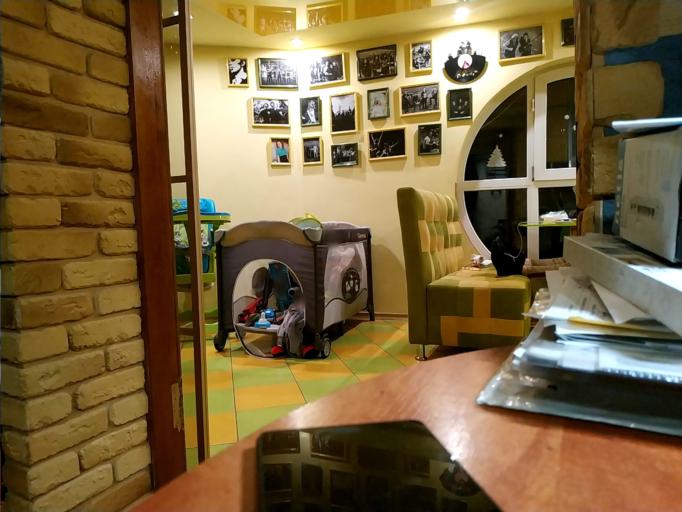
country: RU
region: Orjol
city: Naryshkino
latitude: 53.0462
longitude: 35.6797
